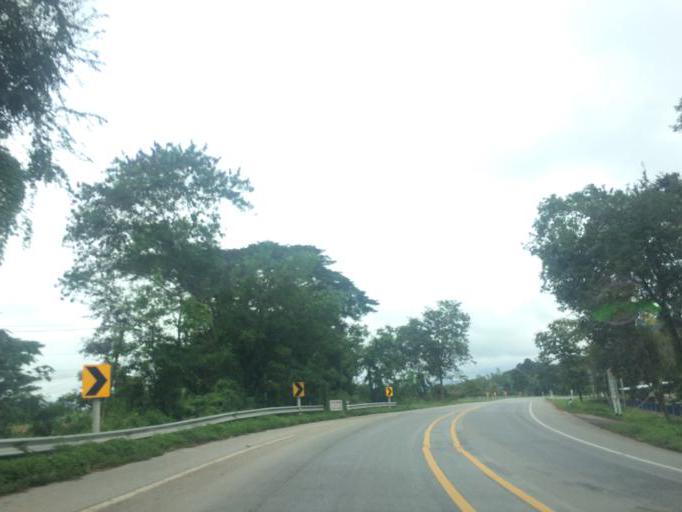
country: TH
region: Chiang Rai
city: Mae Lao
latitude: 19.7475
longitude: 99.6783
